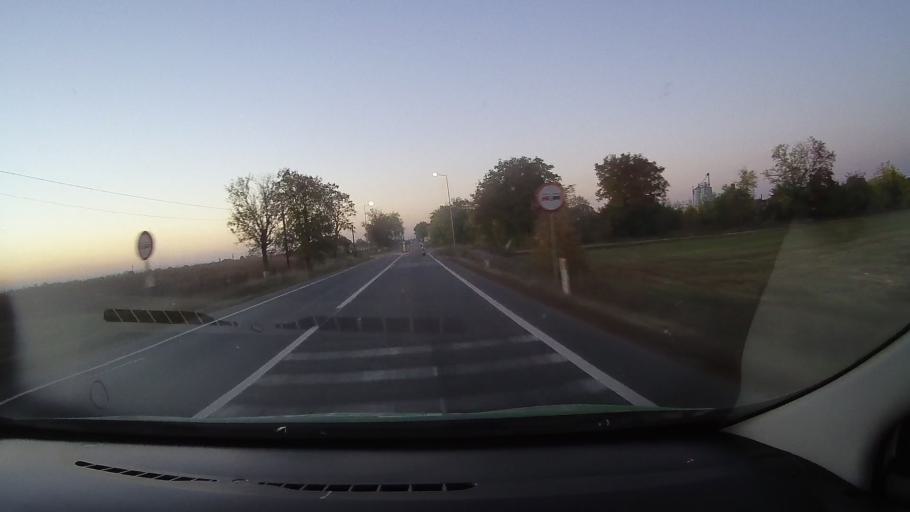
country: RO
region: Bihor
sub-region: Comuna Valea lui Mihai
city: Valea lui Mihai
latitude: 47.5047
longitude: 22.1449
